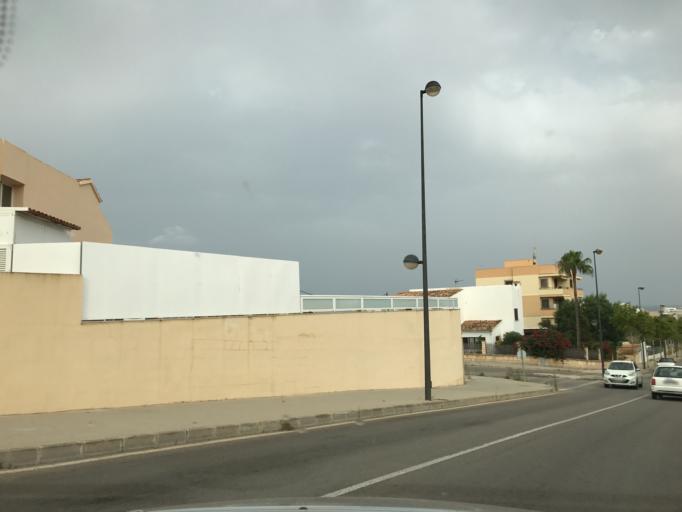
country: ES
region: Balearic Islands
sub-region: Illes Balears
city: Son Servera
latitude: 39.6015
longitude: 3.3695
